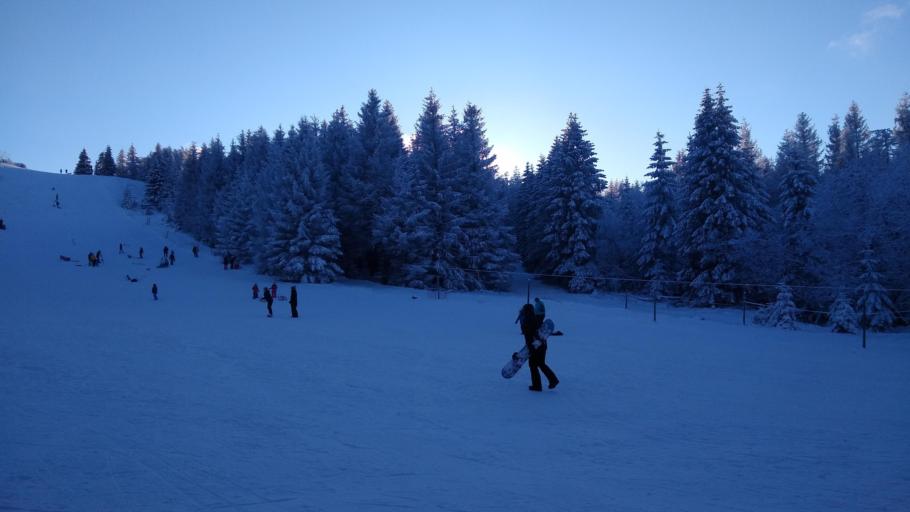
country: DE
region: Lower Saxony
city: Sankt Andreasberg
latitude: 51.7580
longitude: 10.5118
